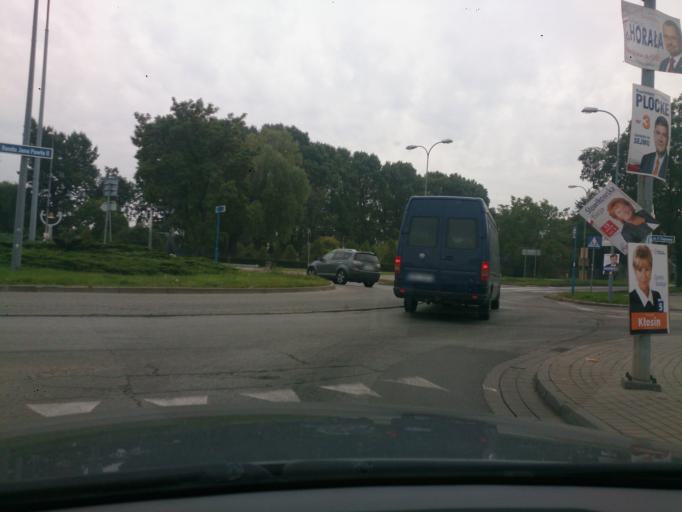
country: PL
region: Pomeranian Voivodeship
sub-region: Powiat wejherowski
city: Rumia
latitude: 54.5786
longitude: 18.3977
